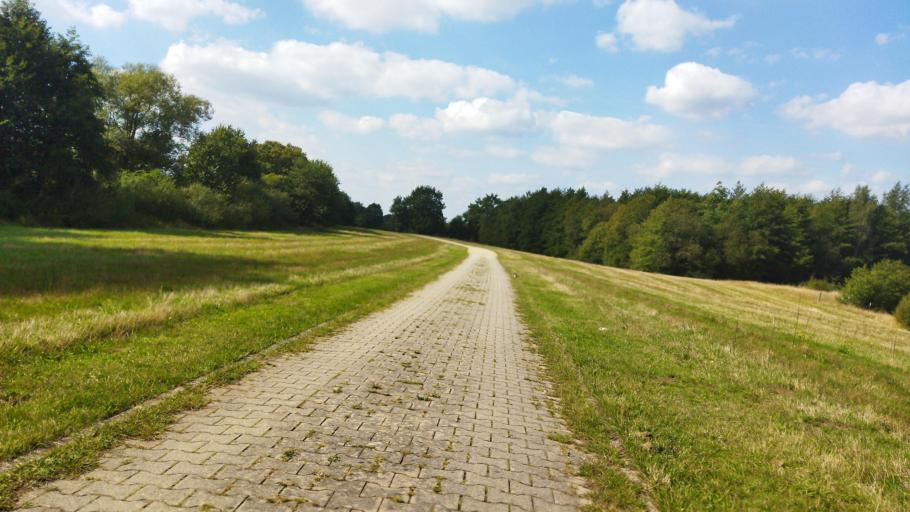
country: DE
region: Lower Saxony
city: Haren
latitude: 52.7825
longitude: 7.2590
